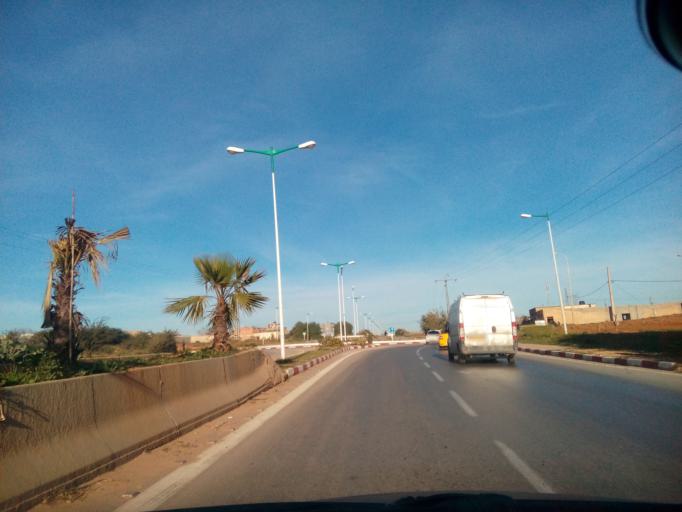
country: DZ
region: Mostaganem
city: Mostaganem
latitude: 35.8691
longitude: 0.1507
